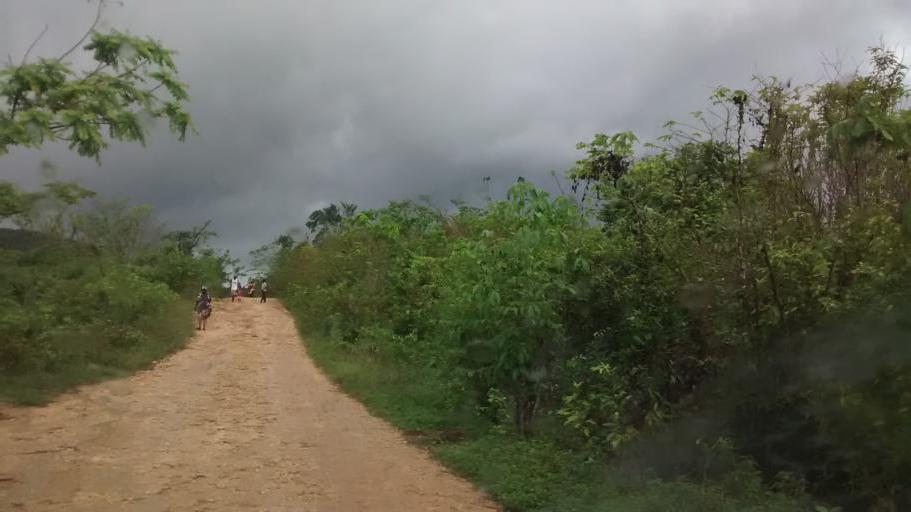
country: HT
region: Grandans
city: Corail
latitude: 18.5380
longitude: -73.9825
